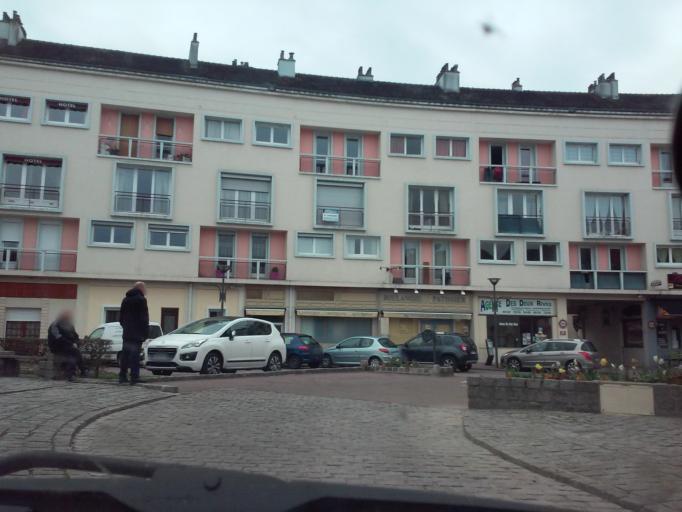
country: FR
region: Haute-Normandie
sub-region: Departement de la Seine-Maritime
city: Caudebec-en-Caux
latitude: 49.5252
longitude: 0.7244
